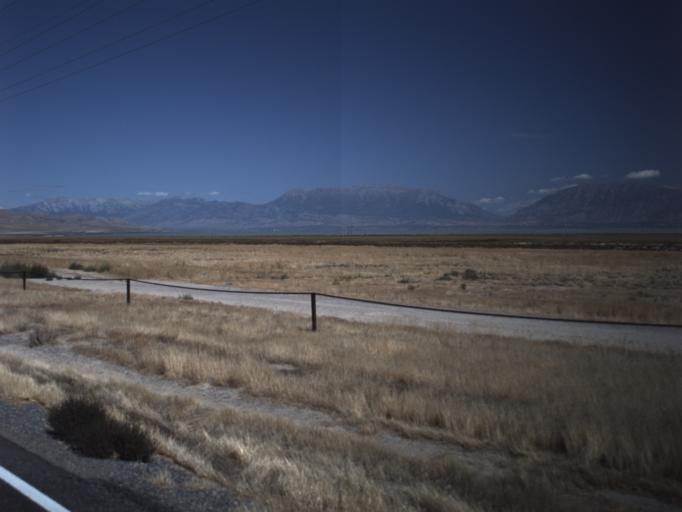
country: US
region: Utah
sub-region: Utah County
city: Genola
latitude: 40.0870
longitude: -111.9588
